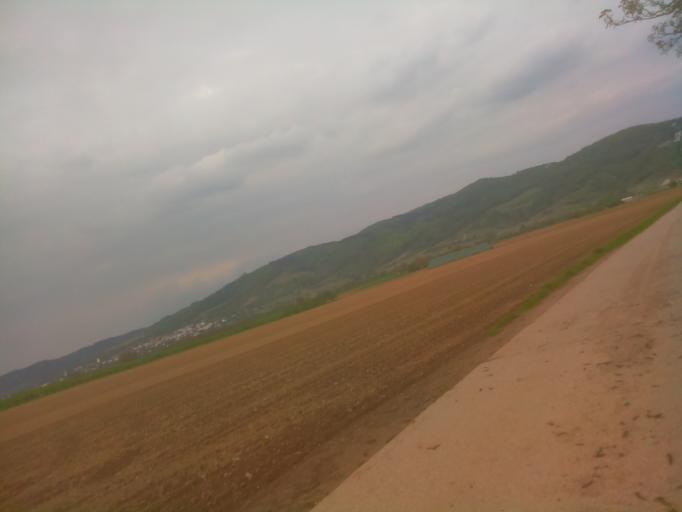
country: DE
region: Baden-Wuerttemberg
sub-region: Karlsruhe Region
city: Schriesheim
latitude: 49.4807
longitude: 8.6443
